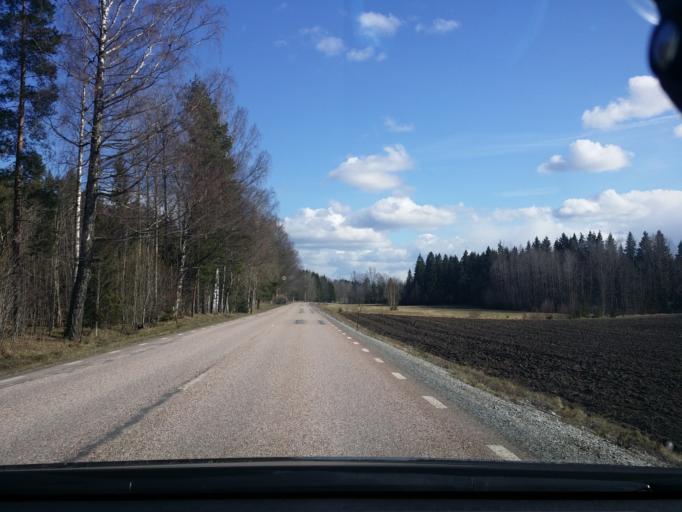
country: SE
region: Vaestmanland
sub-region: Sala Kommun
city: Sala
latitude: 59.9834
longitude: 16.4848
